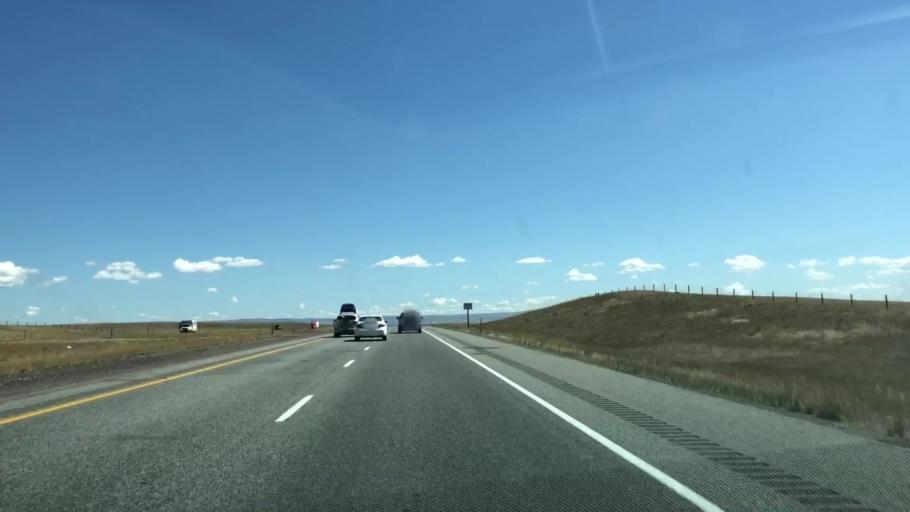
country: US
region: Wyoming
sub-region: Albany County
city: Laramie
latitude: 41.4377
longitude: -105.9254
